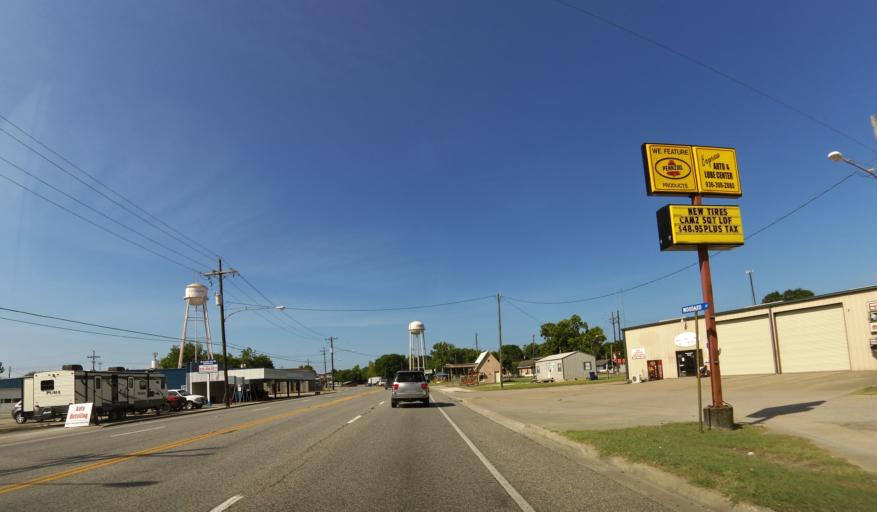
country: US
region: Texas
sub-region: Polk County
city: Corrigan
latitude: 31.0000
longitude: -94.8265
